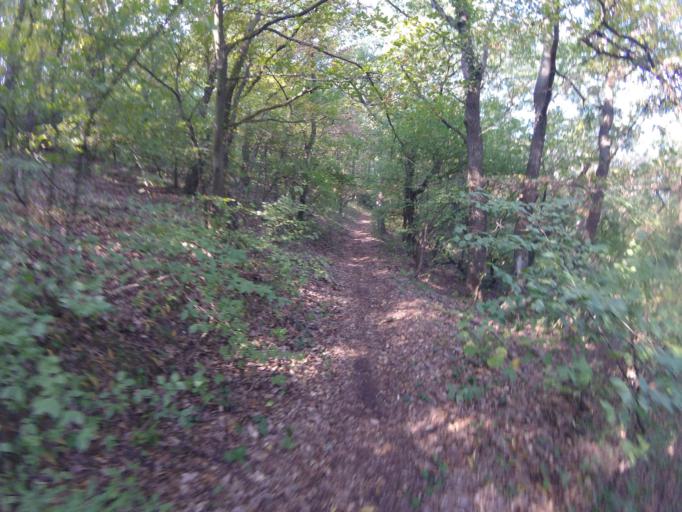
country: HU
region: Gyor-Moson-Sopron
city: Fertorakos
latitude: 47.7223
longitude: 16.6339
